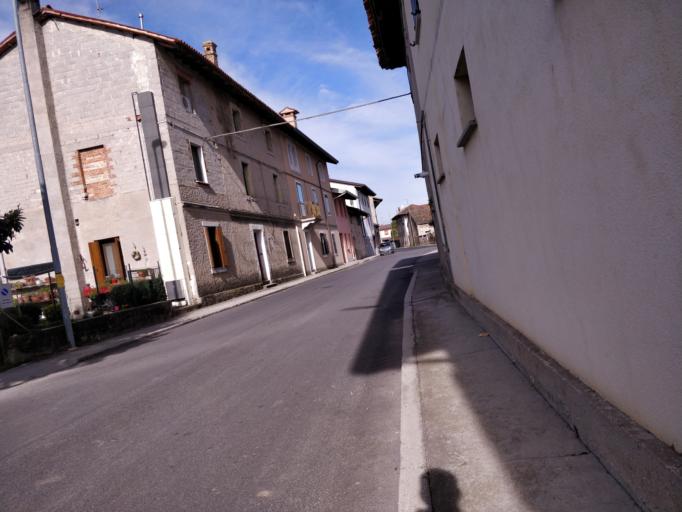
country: IT
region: Friuli Venezia Giulia
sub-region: Provincia di Udine
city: Bertiolo
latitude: 45.9431
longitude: 13.0242
